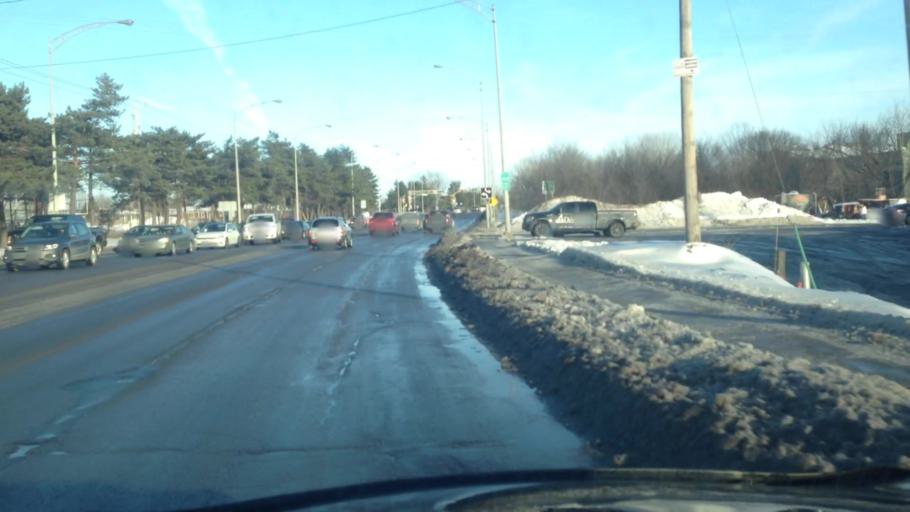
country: CA
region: Quebec
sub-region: Laurentides
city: Saint-Jerome
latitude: 45.7623
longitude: -73.9906
